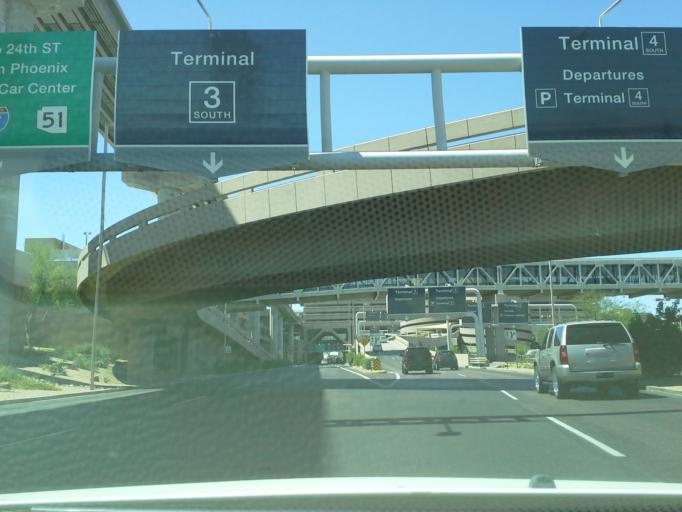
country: US
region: Arizona
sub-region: Maricopa County
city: Tempe Junction
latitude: 33.4350
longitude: -111.9929
